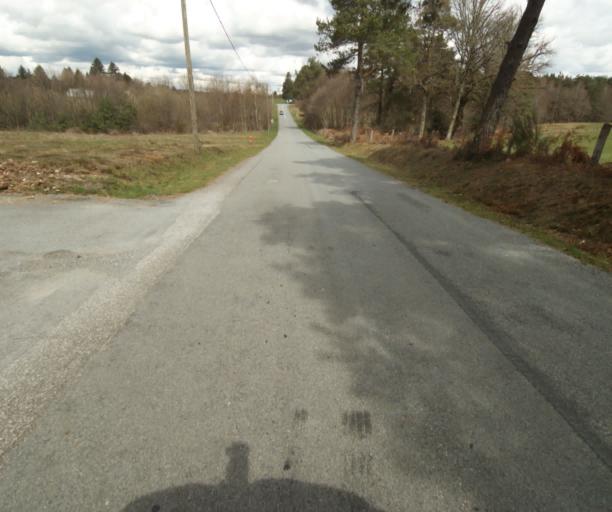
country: FR
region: Limousin
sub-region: Departement de la Correze
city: Correze
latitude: 45.3427
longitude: 1.9469
